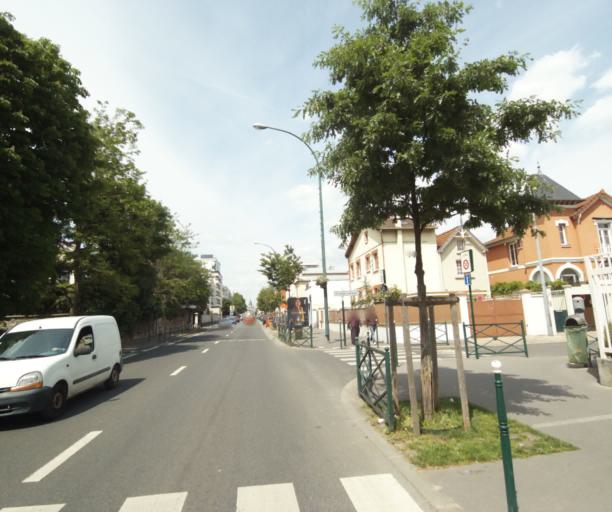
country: FR
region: Ile-de-France
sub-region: Departement des Hauts-de-Seine
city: Colombes
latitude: 48.9189
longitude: 2.2527
